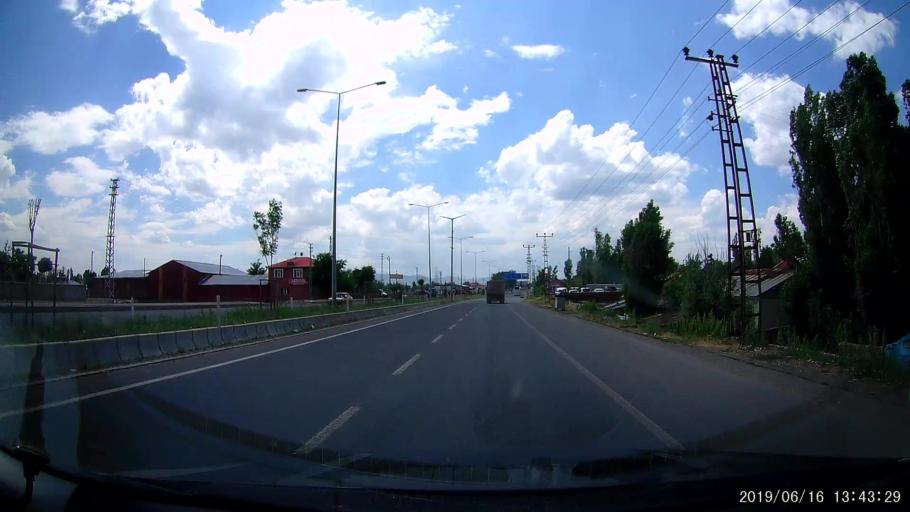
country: TR
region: Agri
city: Agri
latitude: 39.7080
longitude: 43.0546
